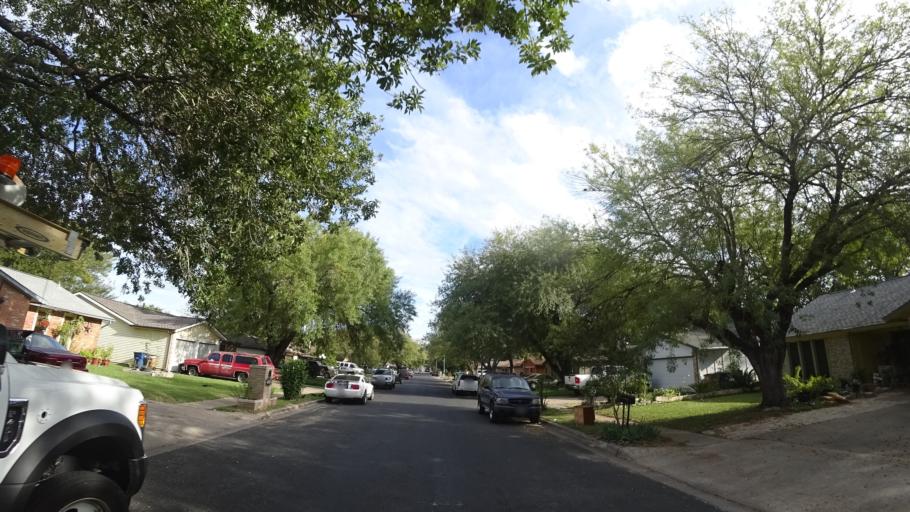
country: US
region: Texas
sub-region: Travis County
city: Onion Creek
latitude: 30.1910
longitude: -97.7521
